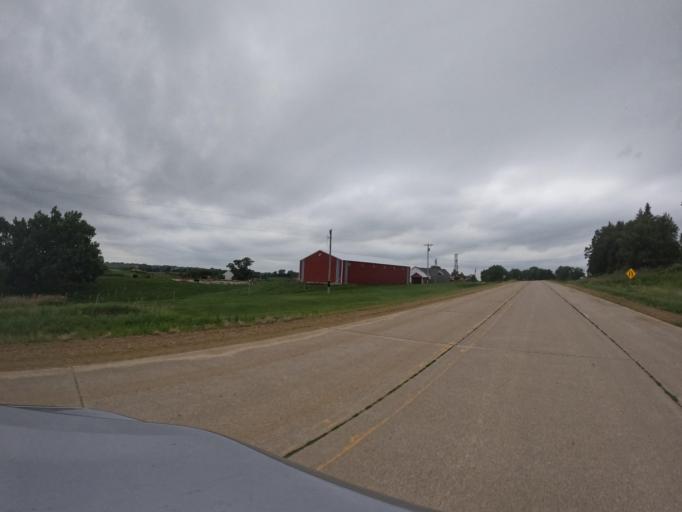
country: US
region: Iowa
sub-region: Jackson County
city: Maquoketa
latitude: 41.9455
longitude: -90.6209
